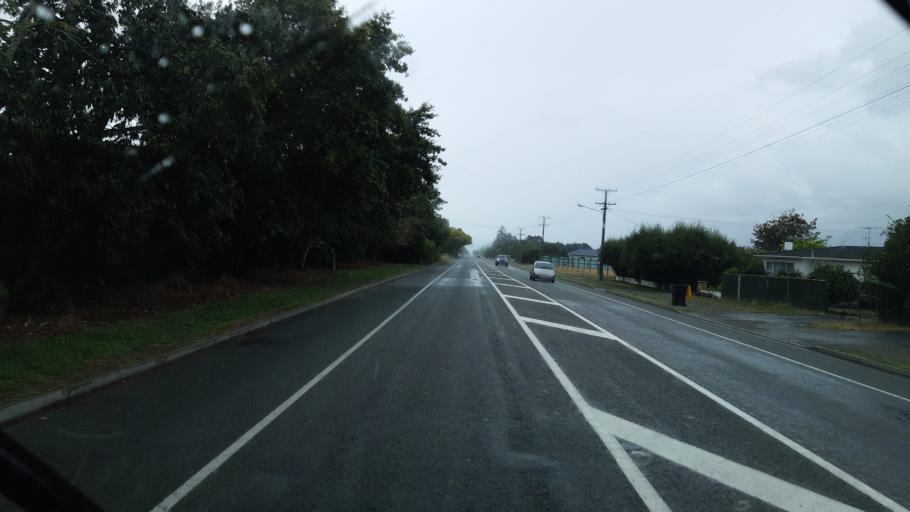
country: NZ
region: Tasman
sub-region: Tasman District
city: Brightwater
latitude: -41.3576
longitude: 173.1484
